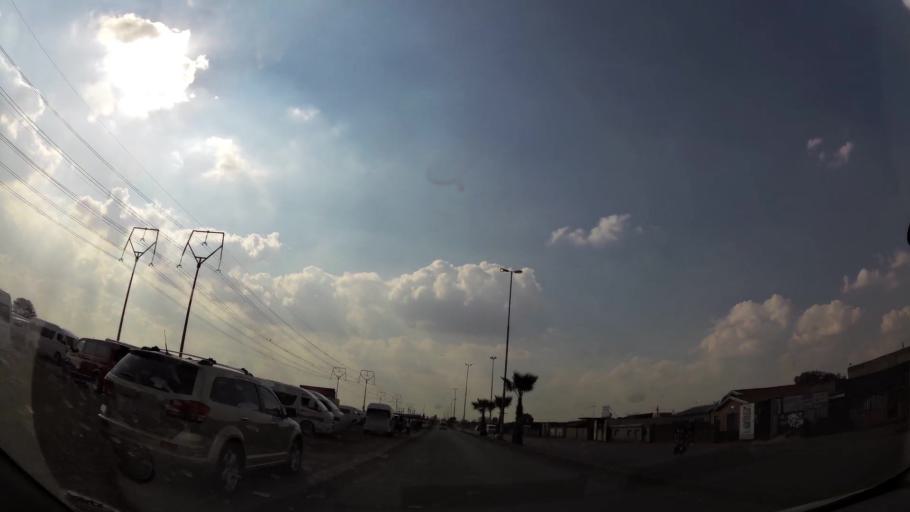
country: ZA
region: Gauteng
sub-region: Ekurhuleni Metropolitan Municipality
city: Germiston
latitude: -26.3257
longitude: 28.1472
